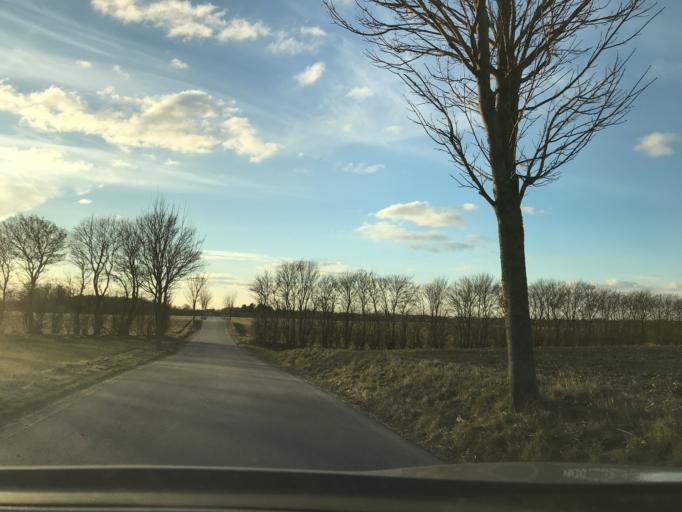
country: DK
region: South Denmark
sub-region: Middelfart Kommune
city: Ejby
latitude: 55.4630
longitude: 9.9348
